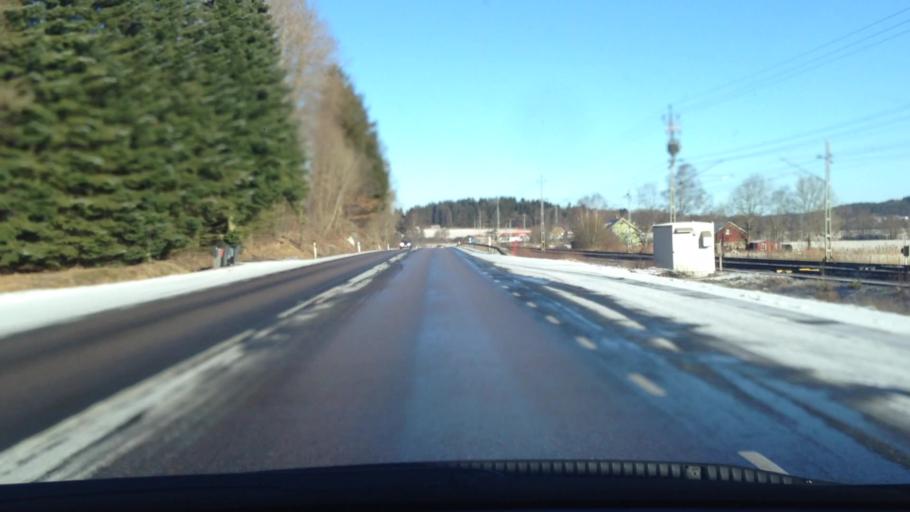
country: SE
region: Vaestra Goetaland
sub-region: Molndal
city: Lindome
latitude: 57.5541
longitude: 12.0904
